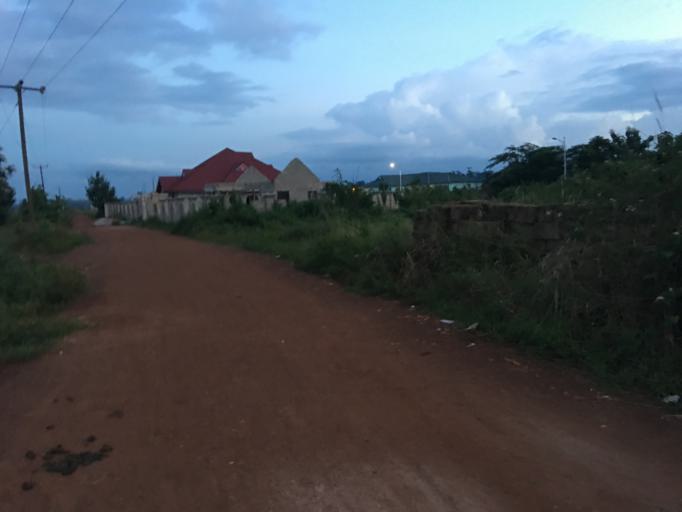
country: GH
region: Western
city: Bibiani
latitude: 6.7850
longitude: -2.5160
